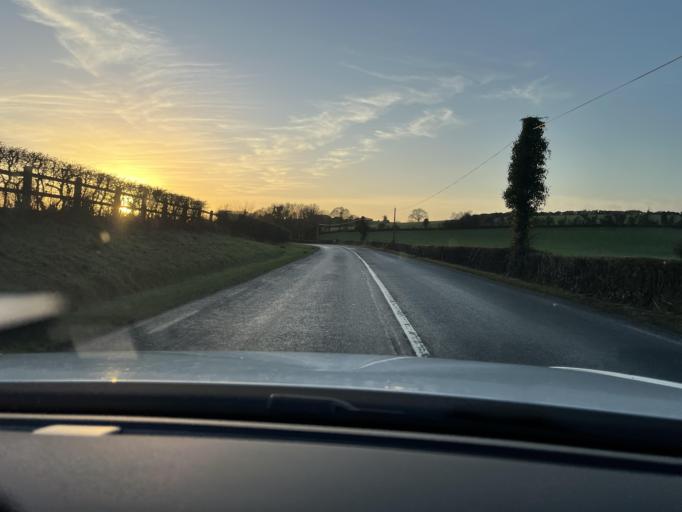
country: IE
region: Ulster
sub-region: An Cabhan
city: Ballyconnell
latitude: 54.0662
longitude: -7.7171
